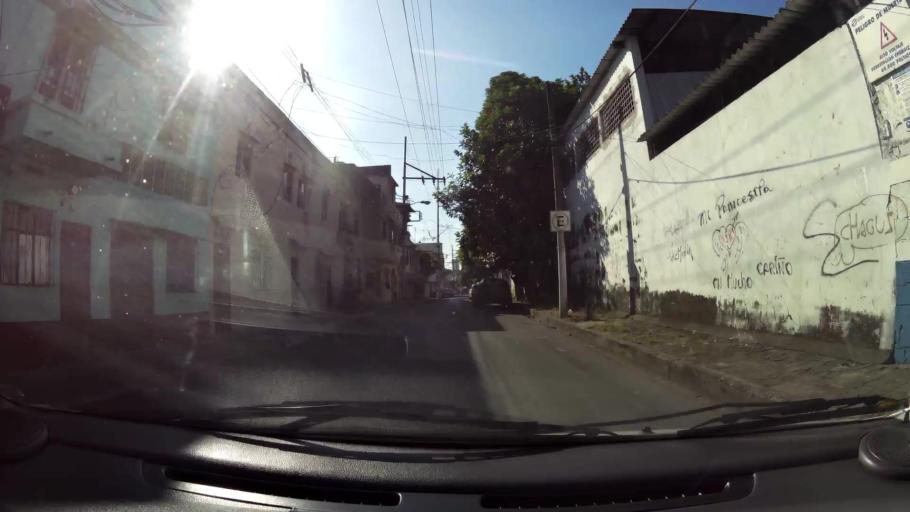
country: EC
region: Guayas
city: Guayaquil
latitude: -2.1773
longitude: -79.8948
